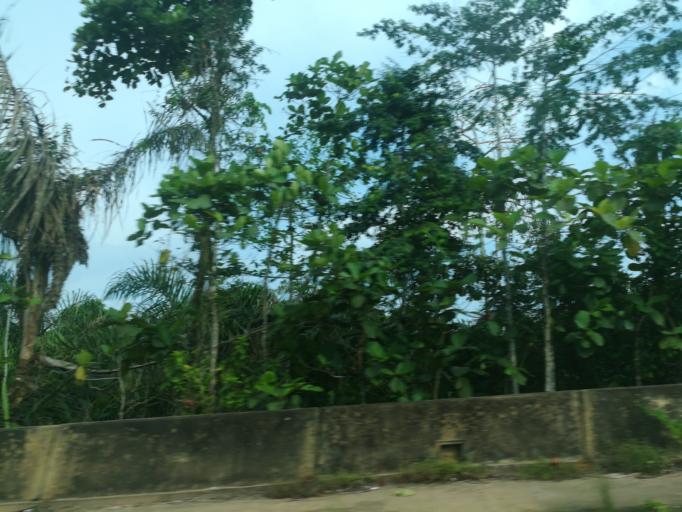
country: NG
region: Lagos
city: Ikorodu
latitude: 6.6282
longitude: 3.6653
